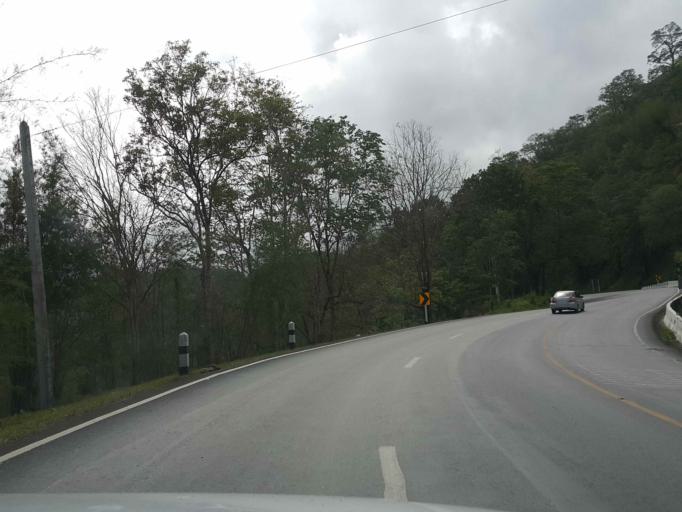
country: TH
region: Tak
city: Tak
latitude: 16.8139
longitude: 98.9697
